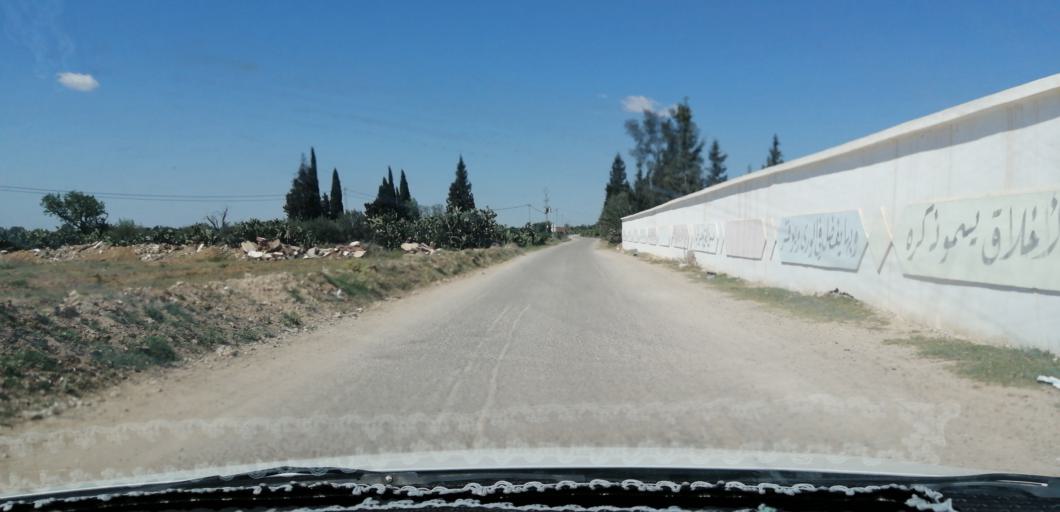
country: TN
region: Al Qayrawan
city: Kairouan
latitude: 35.6337
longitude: 9.9482
